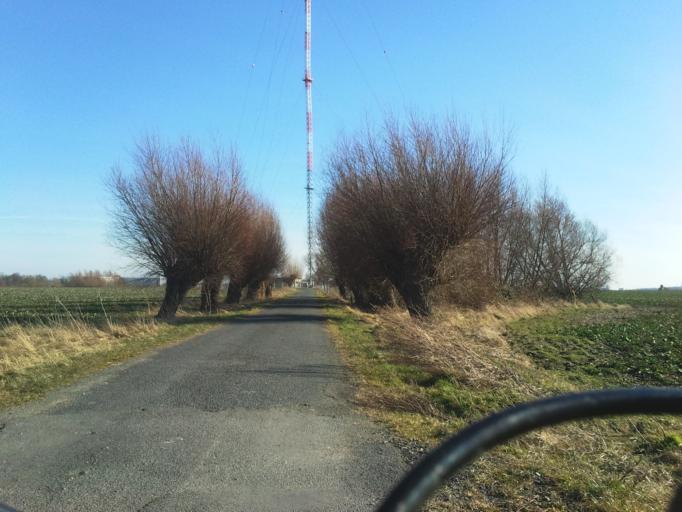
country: DE
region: Mecklenburg-Vorpommern
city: Dierkow-West
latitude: 54.1319
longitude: 12.1230
